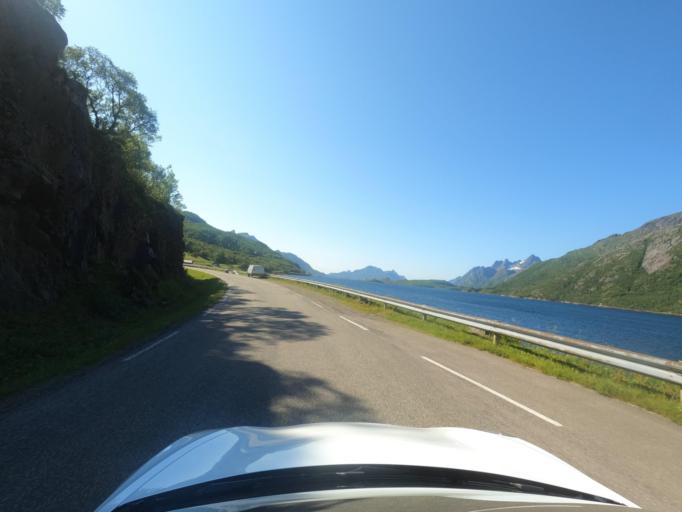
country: NO
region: Nordland
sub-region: Hadsel
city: Stokmarknes
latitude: 68.3845
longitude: 15.0895
